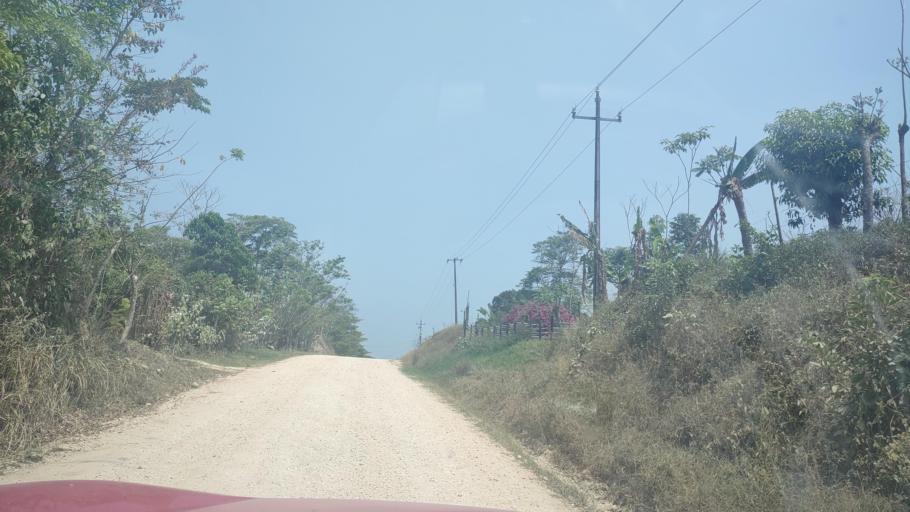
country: MX
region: Tabasco
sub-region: Huimanguillo
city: Francisco Rueda
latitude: 17.6832
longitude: -94.0316
